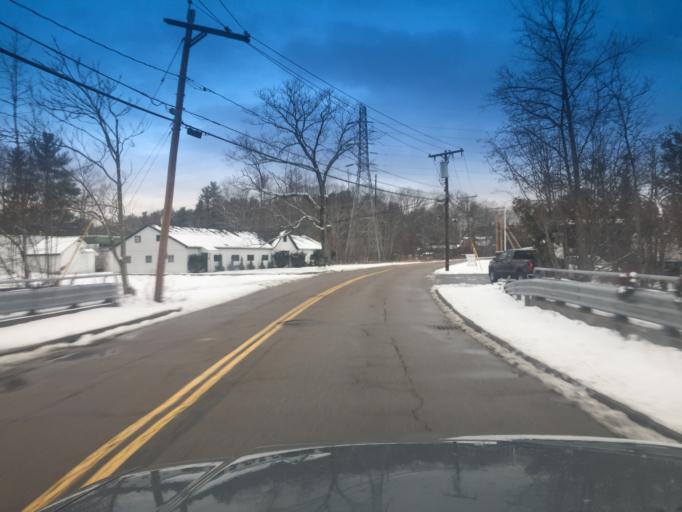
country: US
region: Massachusetts
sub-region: Middlesex County
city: Holliston
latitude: 42.2032
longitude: -71.3991
